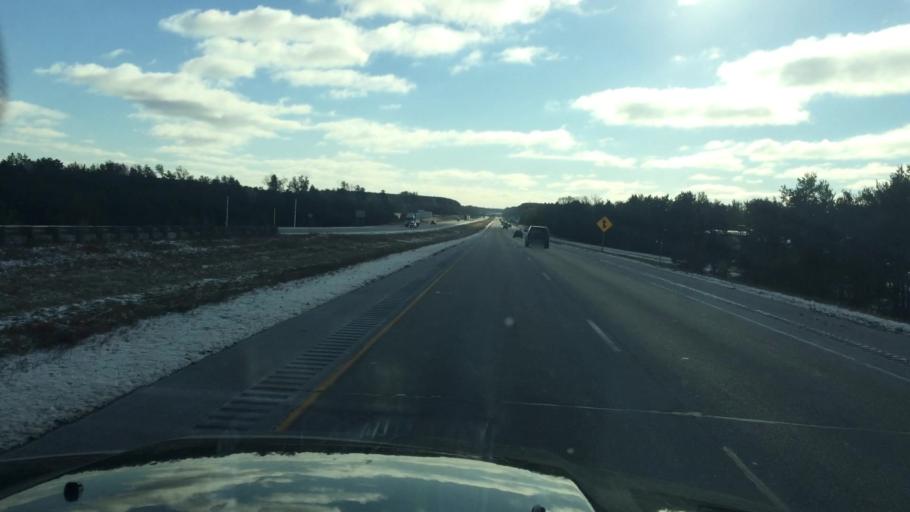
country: US
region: Wisconsin
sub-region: Portage County
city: Stevens Point
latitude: 44.5404
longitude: -89.5442
